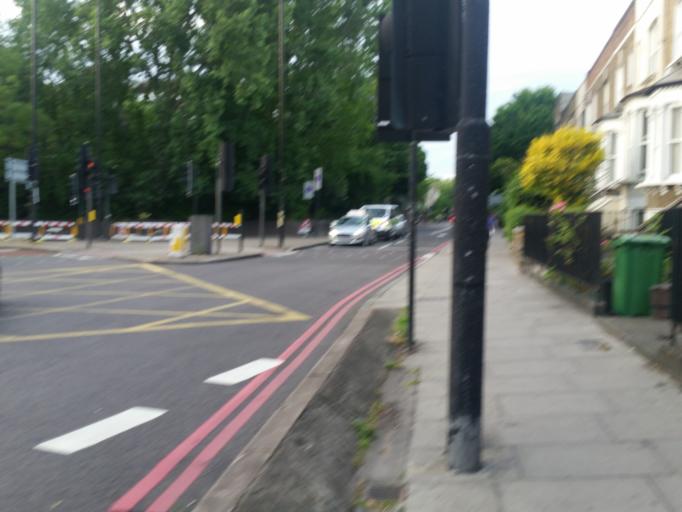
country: GB
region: England
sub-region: Greater London
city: Holloway
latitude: 51.5660
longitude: -0.1337
